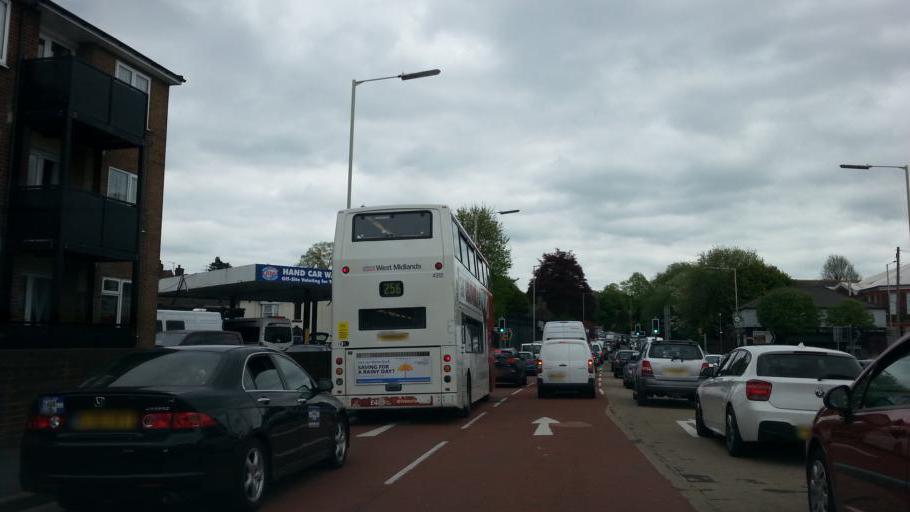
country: GB
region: England
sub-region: Dudley
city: Stourbridge
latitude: 52.4685
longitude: -2.1536
